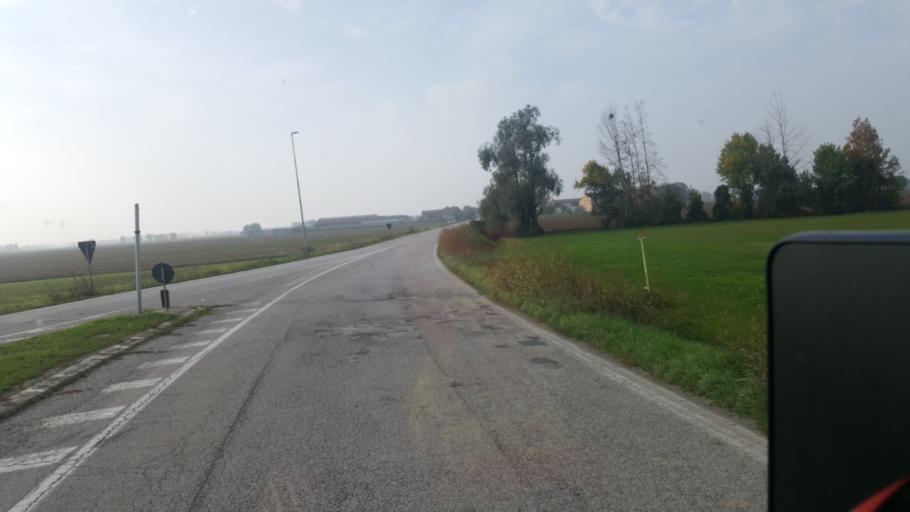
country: IT
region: Lombardy
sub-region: Provincia di Mantova
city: Rodigo
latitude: 45.2198
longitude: 10.6139
